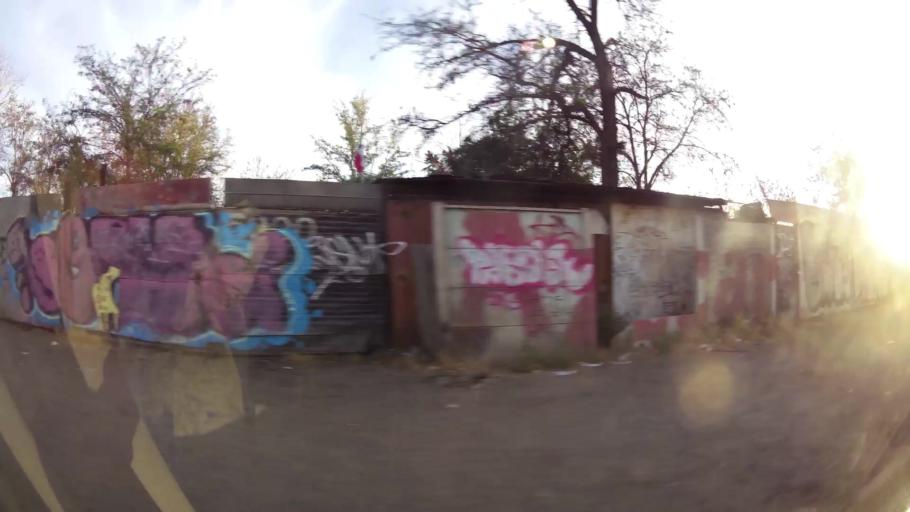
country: CL
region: Santiago Metropolitan
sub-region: Provincia de Santiago
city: Lo Prado
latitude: -33.4092
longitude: -70.7032
